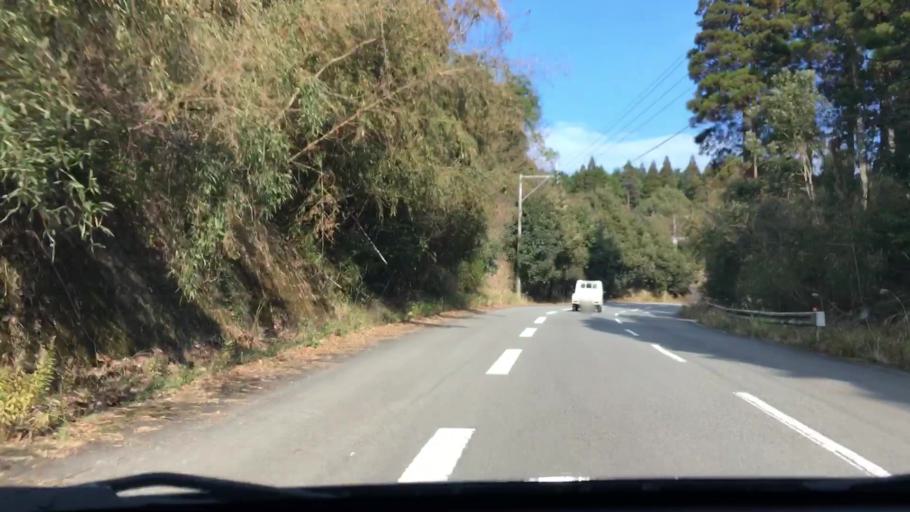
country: JP
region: Miyazaki
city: Nichinan
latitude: 31.5989
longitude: 131.3171
